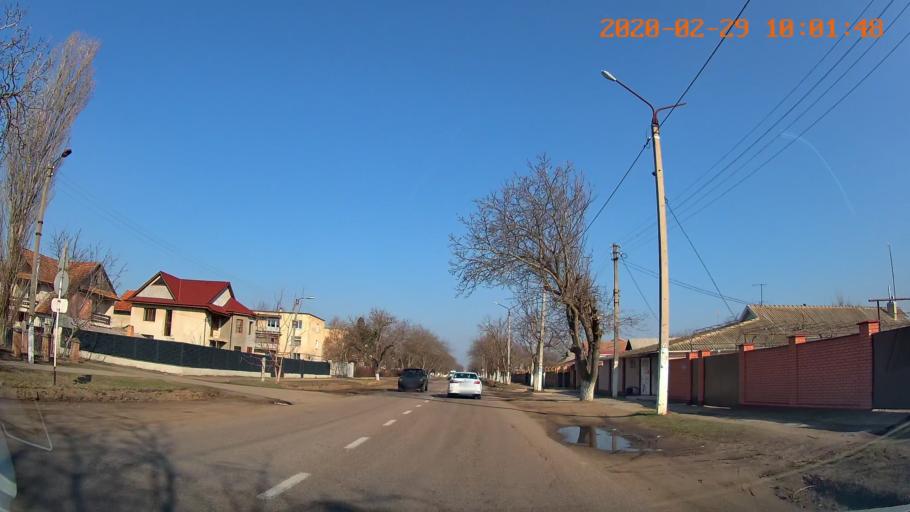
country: MD
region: Telenesti
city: Slobozia
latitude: 46.7778
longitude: 29.6843
